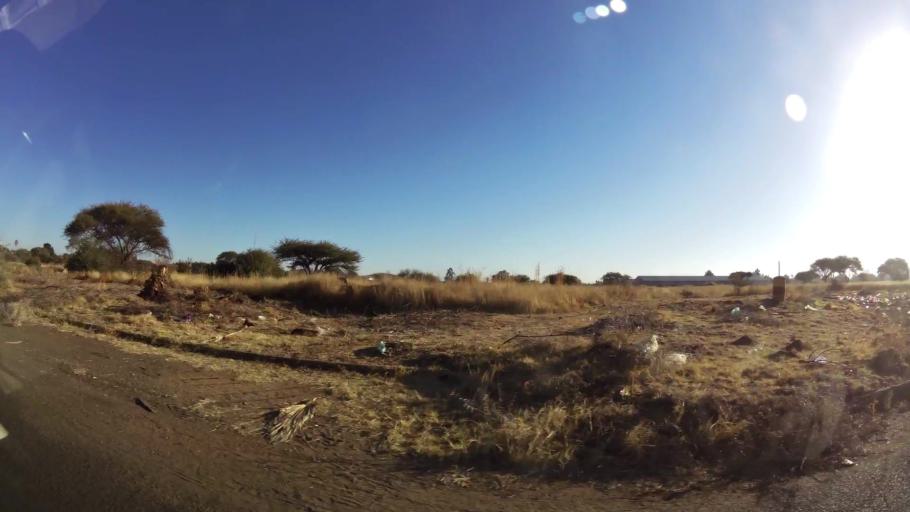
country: ZA
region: Northern Cape
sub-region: Frances Baard District Municipality
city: Kimberley
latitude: -28.7475
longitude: 24.7298
